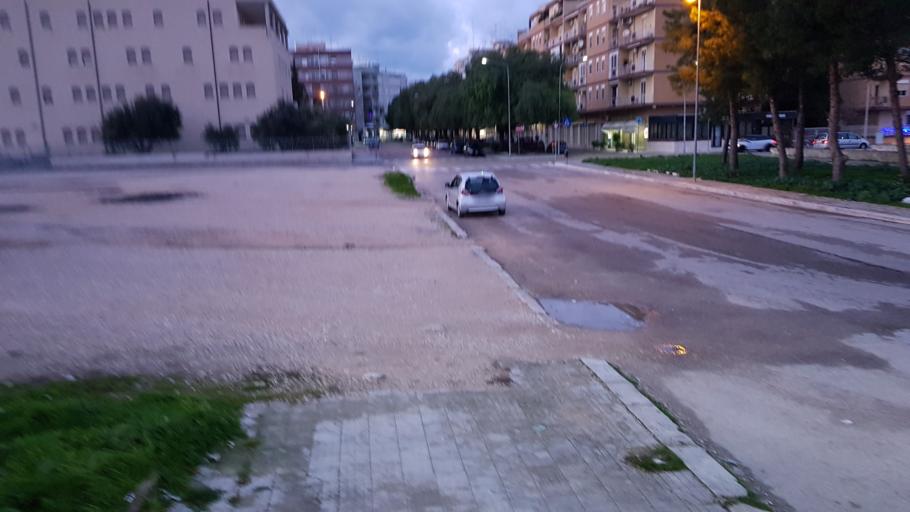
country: IT
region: Apulia
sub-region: Provincia di Brindisi
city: Brindisi
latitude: 40.6233
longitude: 17.9257
